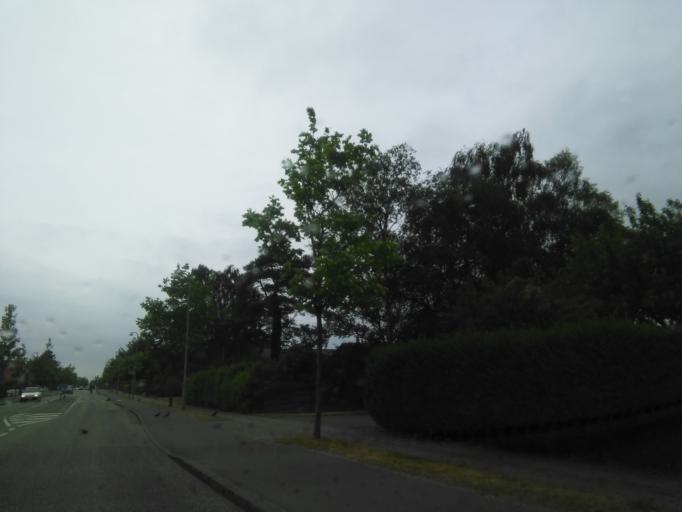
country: DK
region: Capital Region
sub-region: Bornholm Kommune
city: Ronne
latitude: 55.0937
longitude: 14.7249
